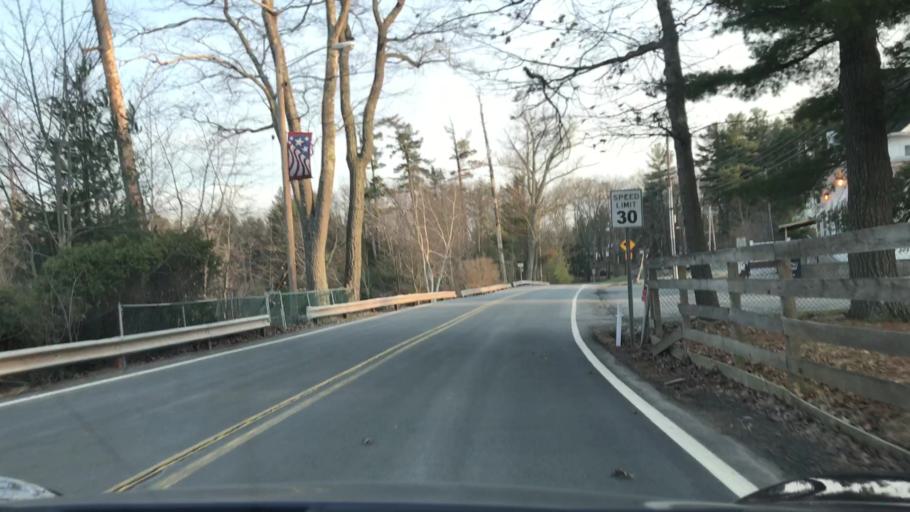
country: US
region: New York
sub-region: Sullivan County
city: Liberty
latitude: 41.6805
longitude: -74.9932
